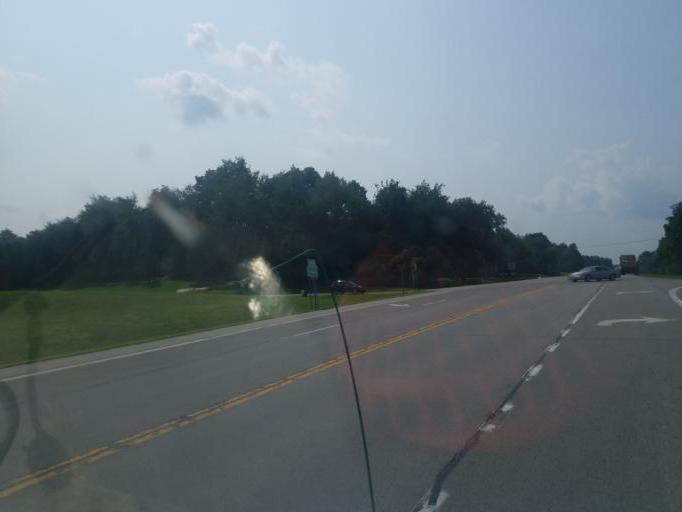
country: US
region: New York
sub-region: Montgomery County
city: Fonda
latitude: 42.9354
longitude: -74.3333
